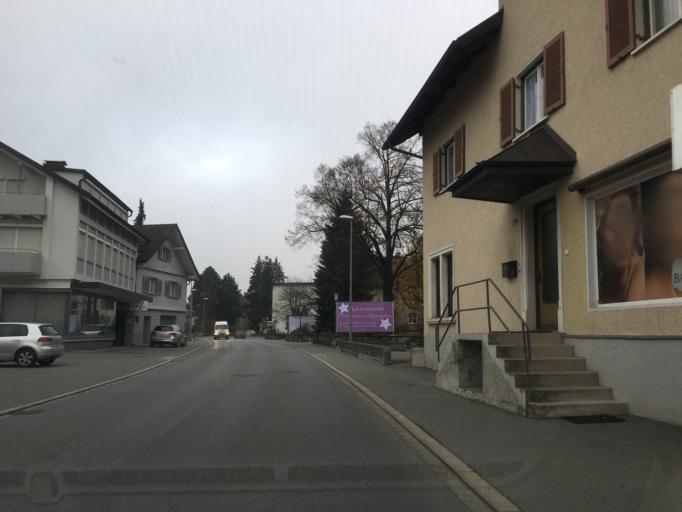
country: AT
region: Vorarlberg
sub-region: Politischer Bezirk Dornbirn
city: Lustenau
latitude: 47.4349
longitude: 9.6565
